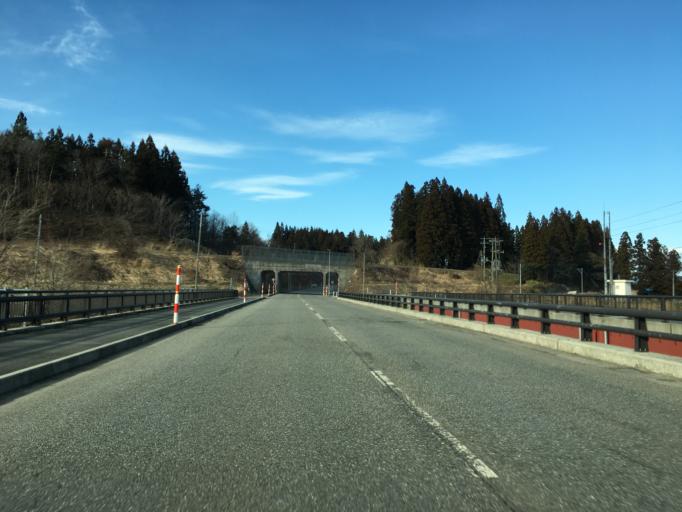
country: JP
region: Yamagata
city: Nagai
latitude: 38.0190
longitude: 139.9716
